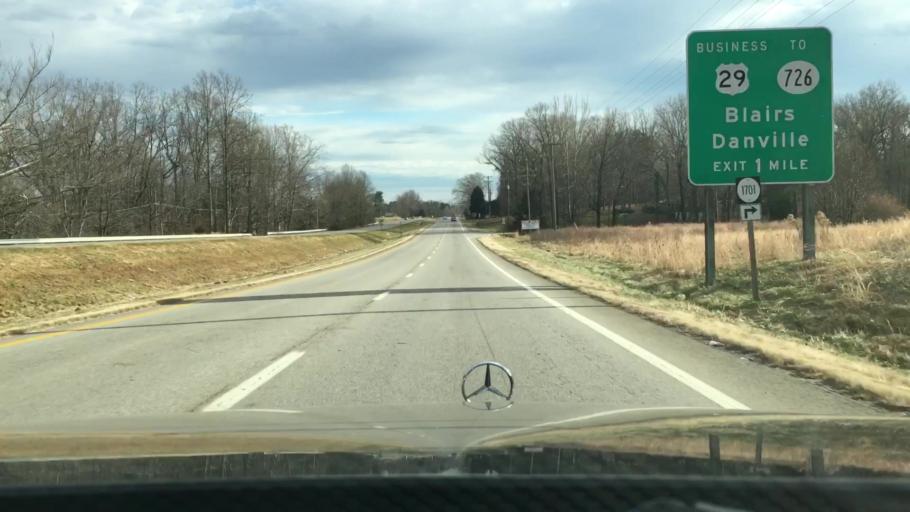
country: US
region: Virginia
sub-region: Pittsylvania County
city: Mount Hermon
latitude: 36.7166
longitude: -79.3798
